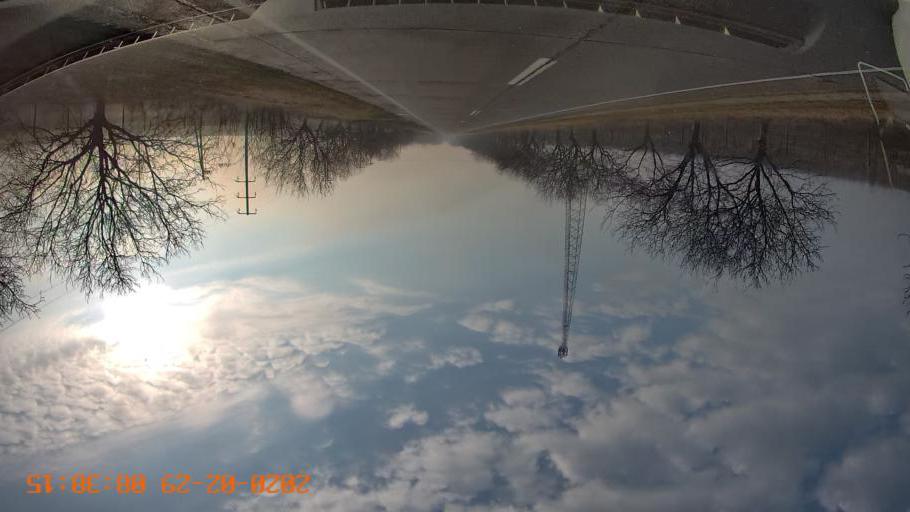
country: MD
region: Anenii Noi
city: Varnita
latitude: 46.9216
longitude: 29.3747
